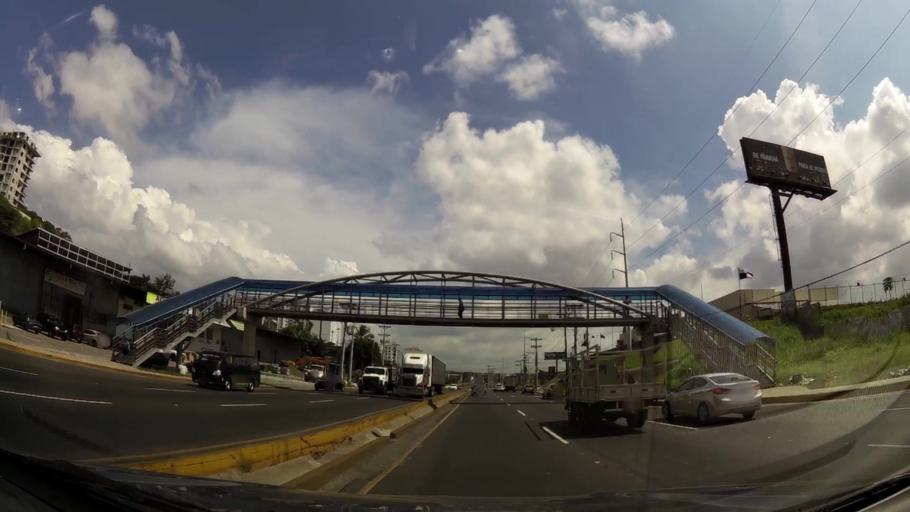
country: PA
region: Panama
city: San Miguelito
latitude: 9.0449
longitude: -79.4694
